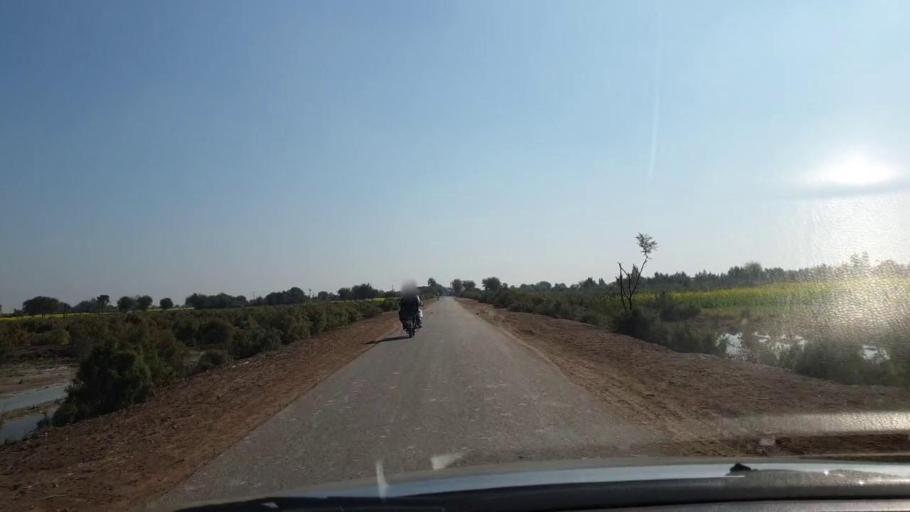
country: PK
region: Sindh
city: Jhol
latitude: 25.9333
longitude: 68.9163
